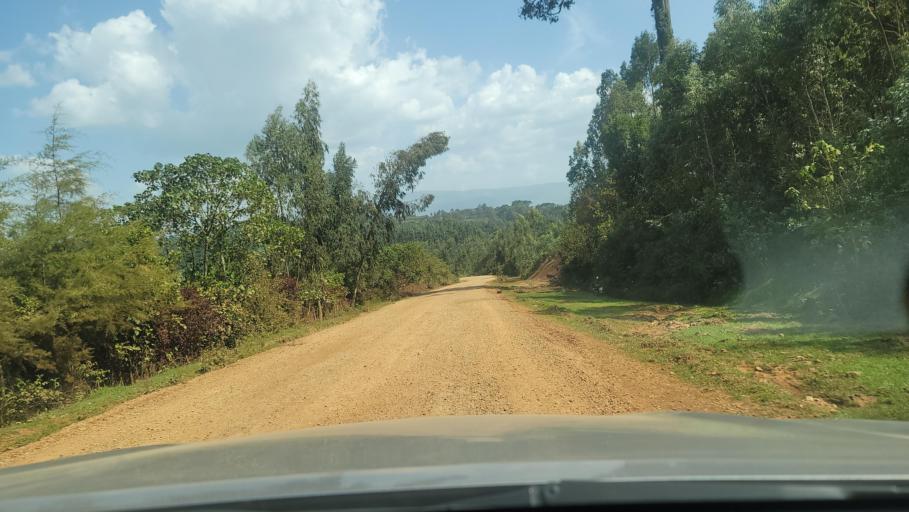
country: ET
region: Oromiya
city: Agaro
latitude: 7.8008
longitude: 36.4567
